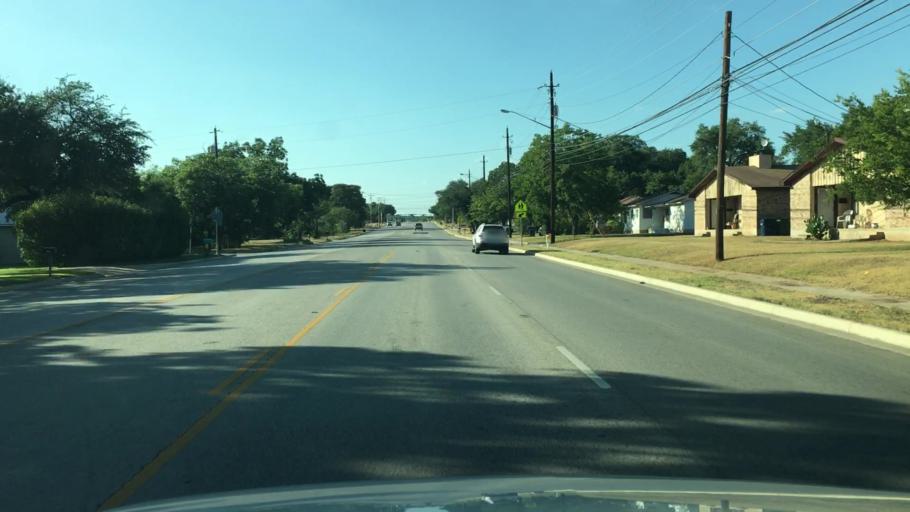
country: US
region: Texas
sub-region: Burnet County
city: Burnet
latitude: 30.7728
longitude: -98.2324
